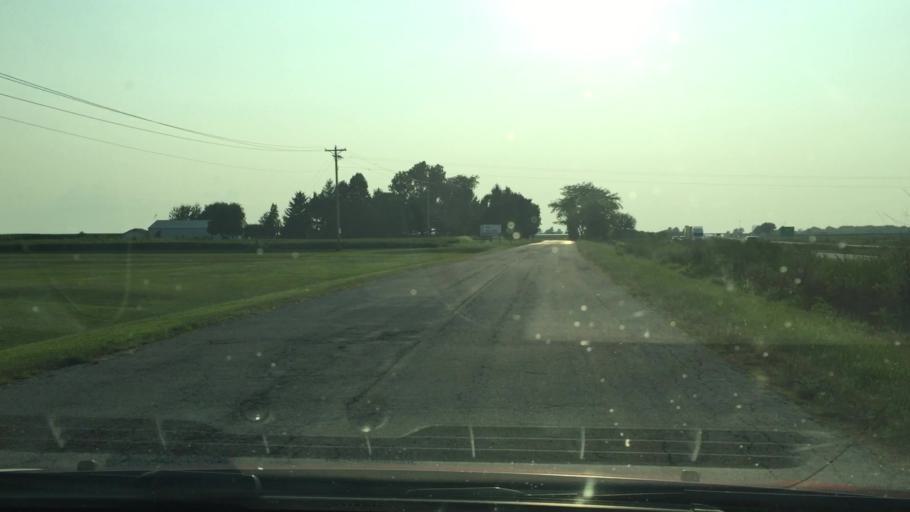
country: US
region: Illinois
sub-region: Bureau County
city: Ladd
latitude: 41.3641
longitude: -89.1982
